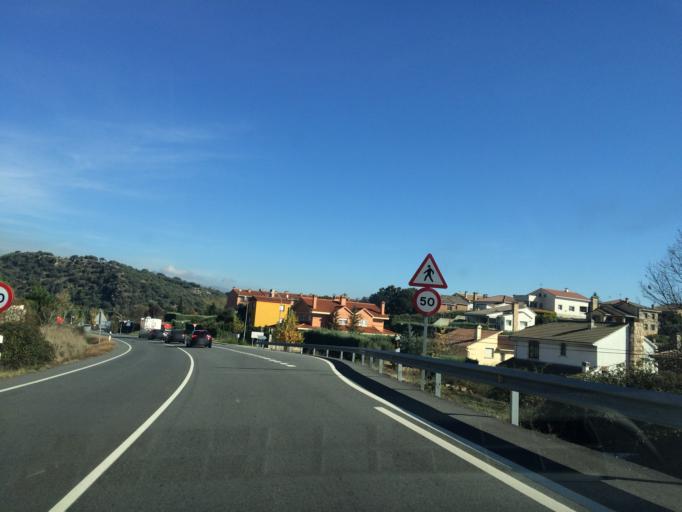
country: ES
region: Madrid
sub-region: Provincia de Madrid
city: Guadalix de la Sierra
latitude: 40.7841
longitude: -3.7085
